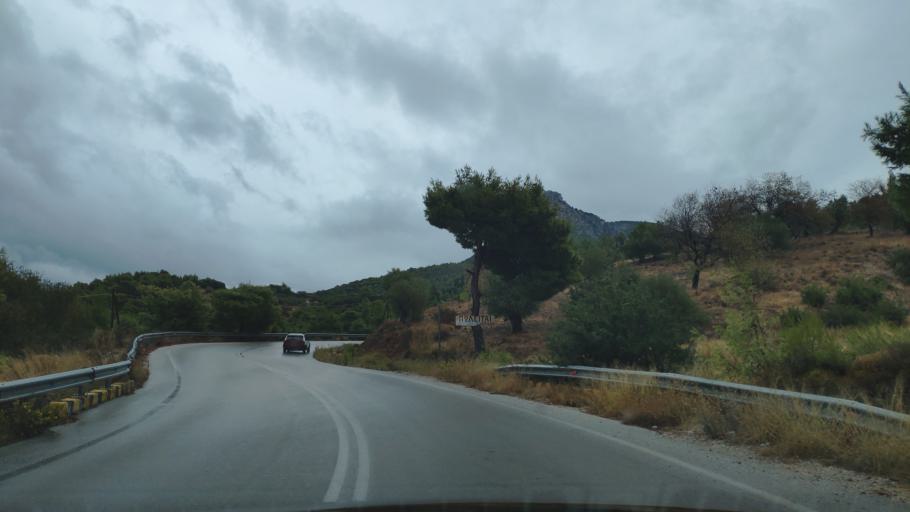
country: GR
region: Peloponnese
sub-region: Nomos Korinthias
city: Perachora
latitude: 38.0074
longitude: 22.9397
